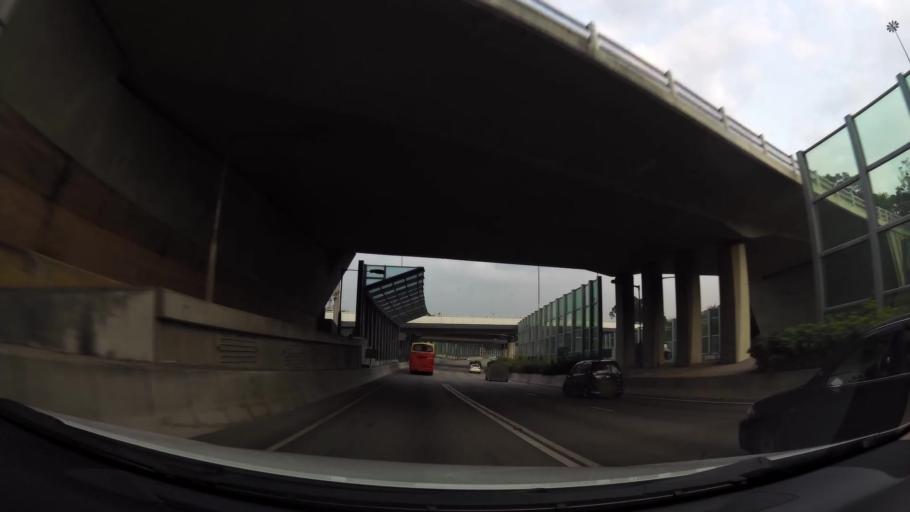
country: HK
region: Tai Po
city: Tai Po
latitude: 22.4452
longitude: 114.1764
